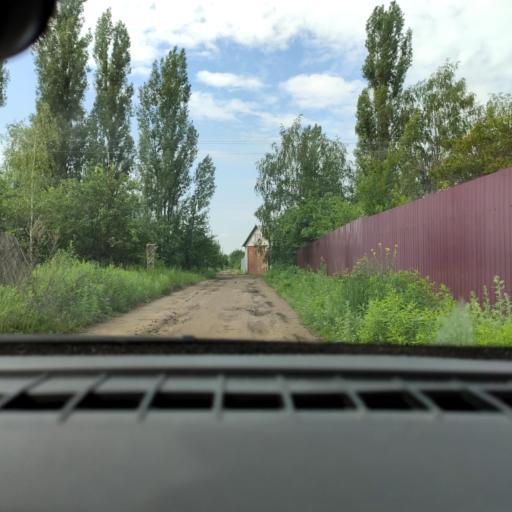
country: RU
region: Voronezj
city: Maslovka
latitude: 51.5015
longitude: 39.1982
